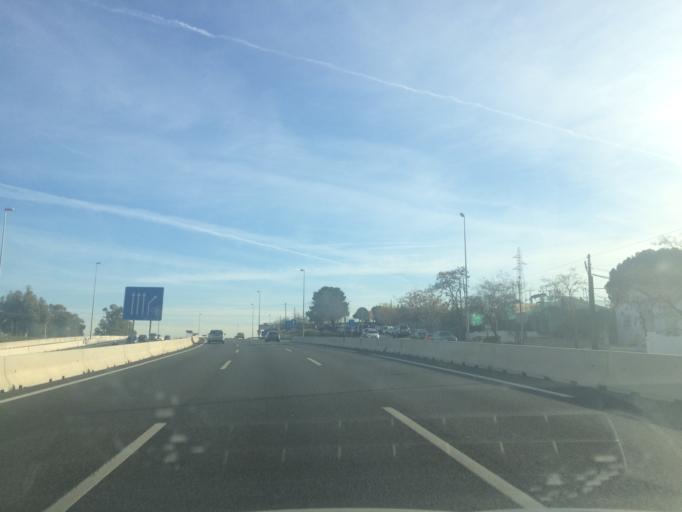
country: ES
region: Madrid
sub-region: Provincia de Madrid
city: Tres Cantos
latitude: 40.5538
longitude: -3.7087
